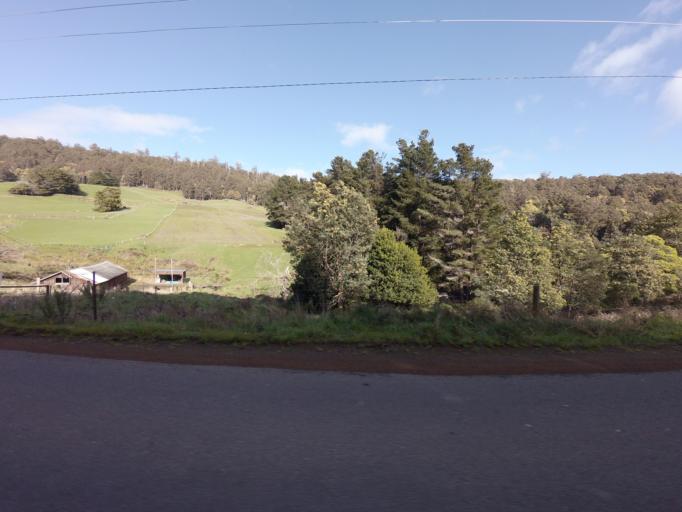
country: AU
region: Tasmania
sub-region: Huon Valley
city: Geeveston
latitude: -43.2384
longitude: 146.9914
